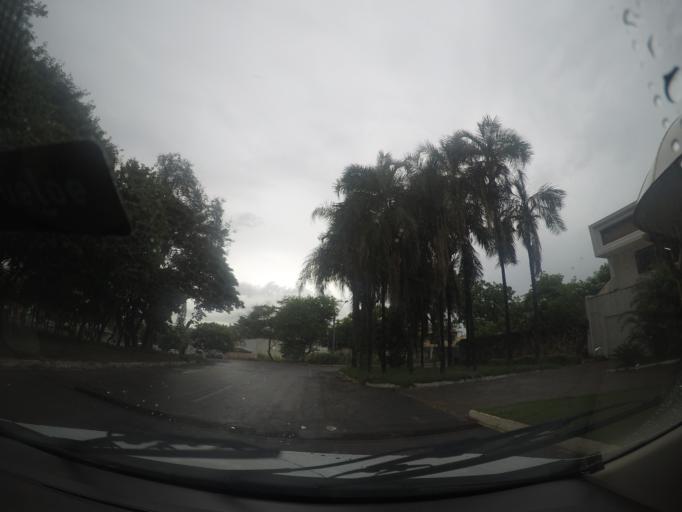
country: BR
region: Goias
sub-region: Goiania
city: Goiania
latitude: -16.6499
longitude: -49.2292
